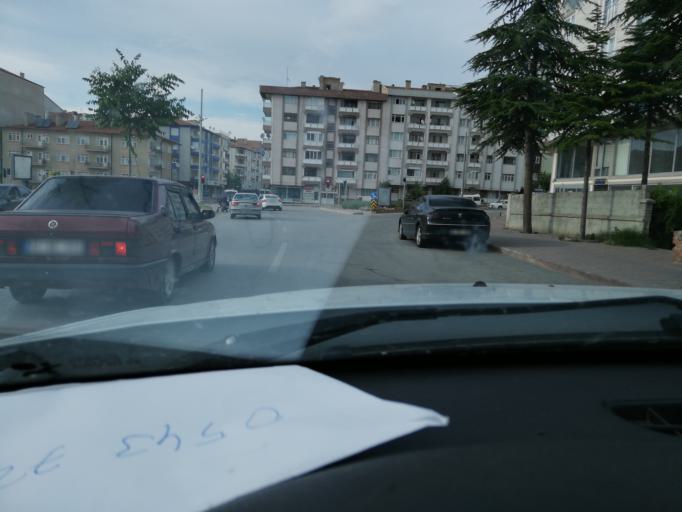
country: TR
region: Kirsehir
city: Kirsehir
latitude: 39.1394
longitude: 34.1606
